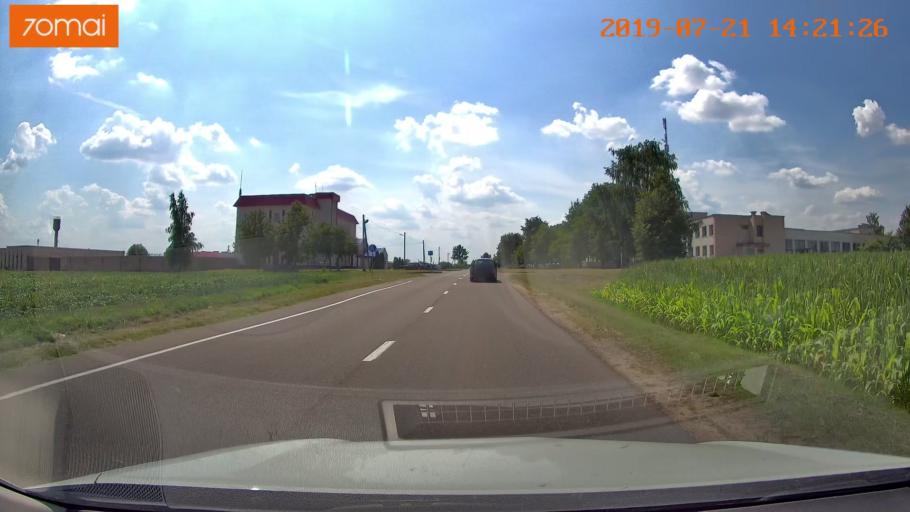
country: BY
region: Grodnenskaya
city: Karelichy
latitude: 53.5765
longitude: 26.1451
